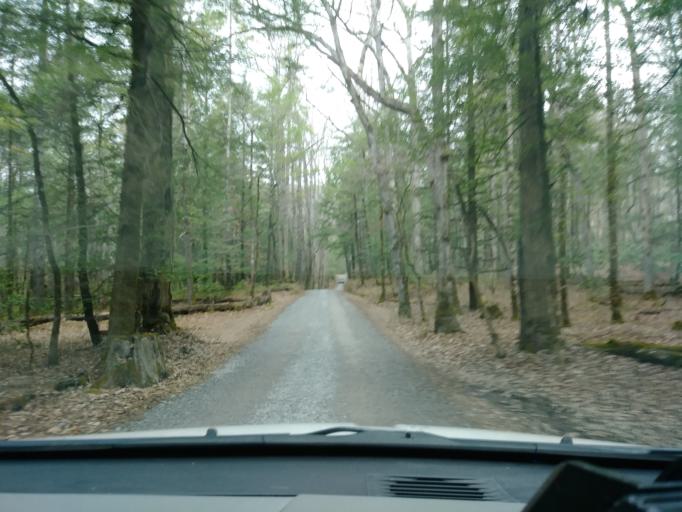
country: US
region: Tennessee
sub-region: Blount County
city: Wildwood
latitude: 35.6043
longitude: -83.8119
